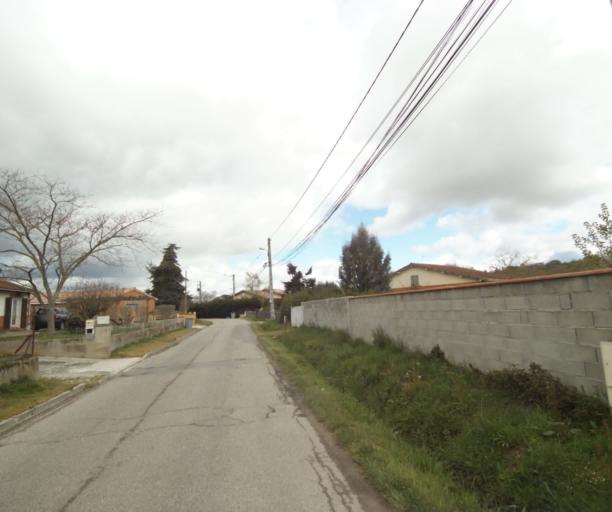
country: FR
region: Midi-Pyrenees
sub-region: Departement de l'Ariege
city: Saverdun
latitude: 43.2223
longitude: 1.5723
